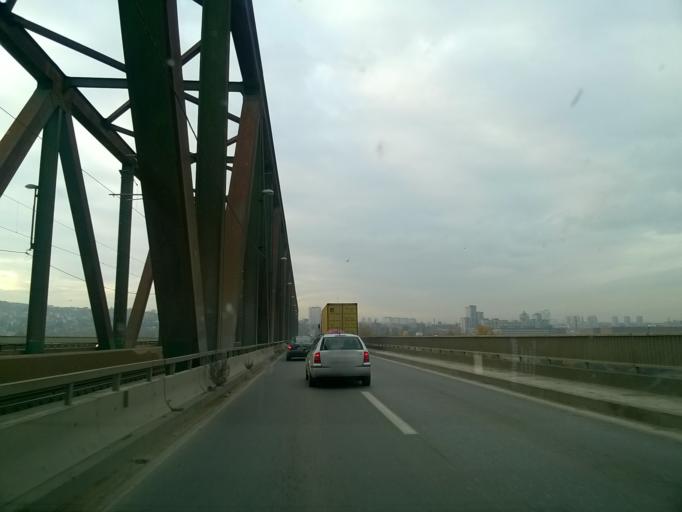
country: RS
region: Central Serbia
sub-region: Belgrade
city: Palilula
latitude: 44.8273
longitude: 20.4918
